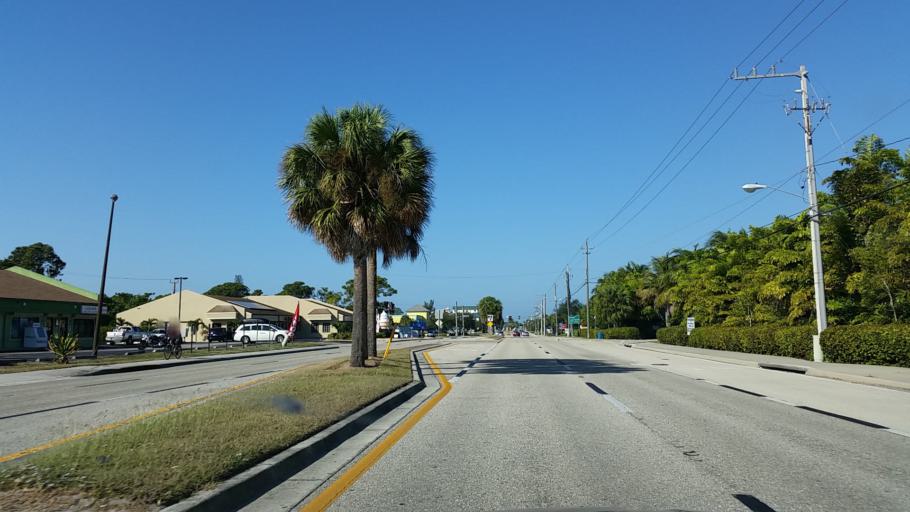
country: US
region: Florida
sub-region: Lee County
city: Bonita Springs
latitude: 26.3305
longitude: -81.8245
